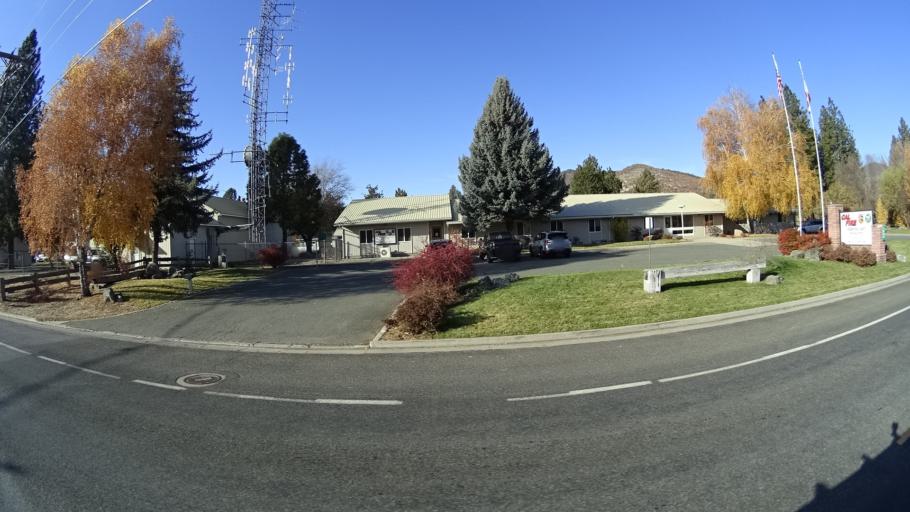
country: US
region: California
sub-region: Siskiyou County
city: Yreka
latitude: 41.7024
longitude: -122.6406
